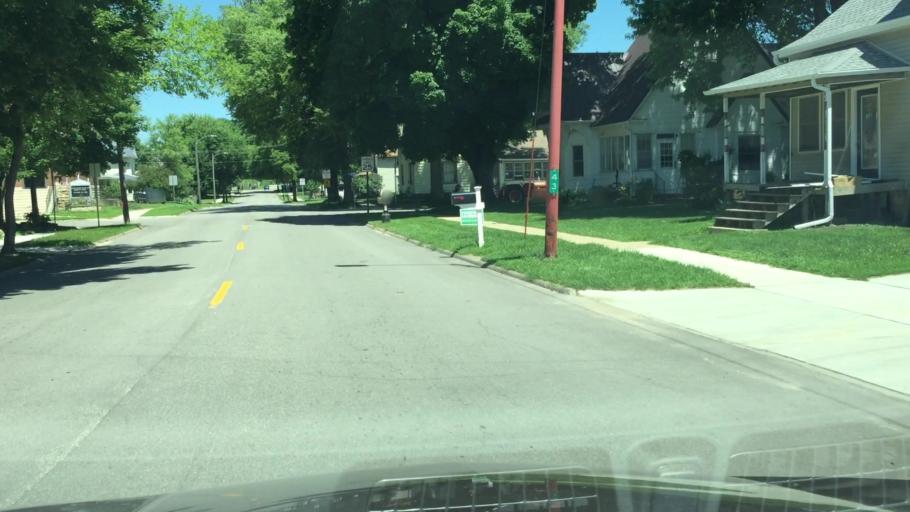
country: US
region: Iowa
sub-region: Cedar County
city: Mechanicsville
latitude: 41.9984
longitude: -91.1419
